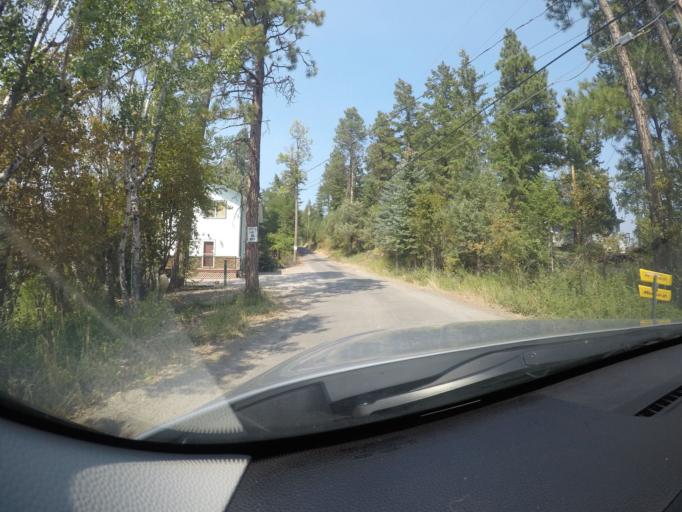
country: US
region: Montana
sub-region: Lake County
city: Polson
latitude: 47.7639
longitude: -114.1418
